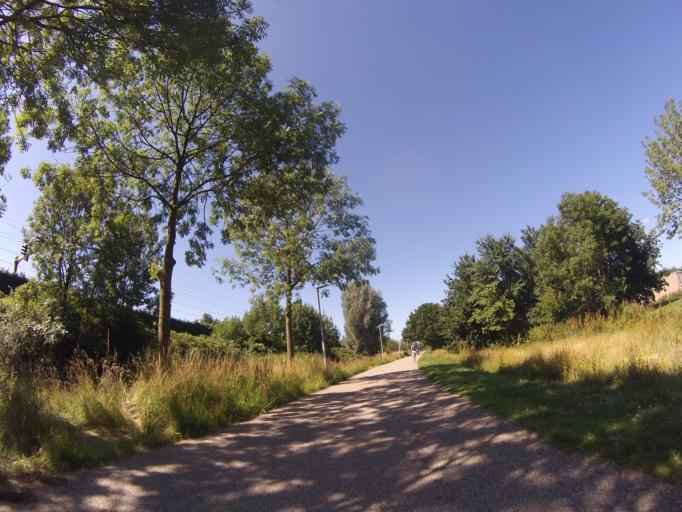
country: NL
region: Utrecht
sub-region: Gemeente Utrecht
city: Utrecht
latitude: 52.1125
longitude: 5.1340
